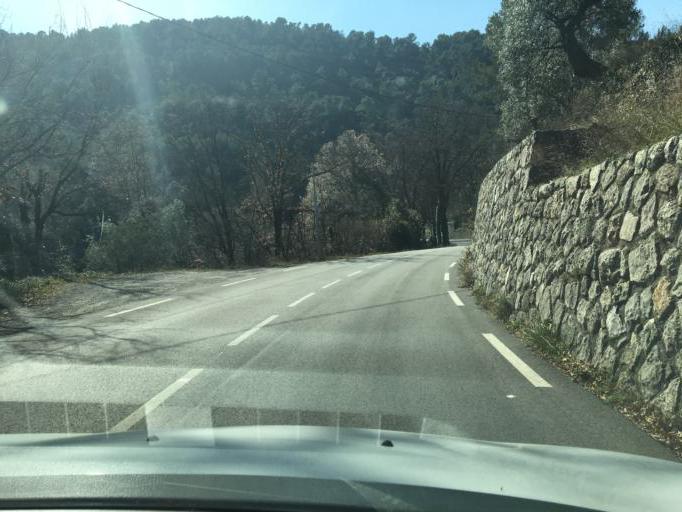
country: FR
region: Provence-Alpes-Cote d'Azur
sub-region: Departement du Var
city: Bargemon
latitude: 43.6156
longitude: 6.5409
